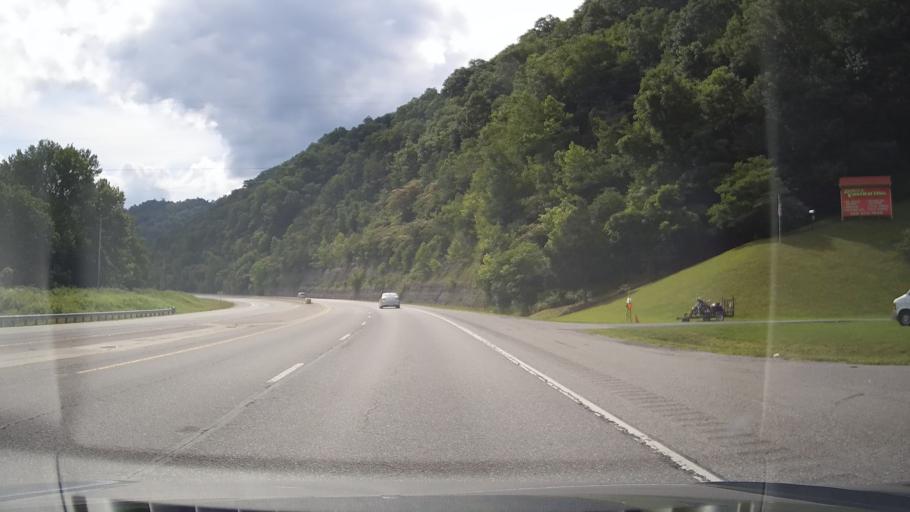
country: US
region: Kentucky
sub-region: Pike County
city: Coal Run Village
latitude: 37.5748
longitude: -82.6464
